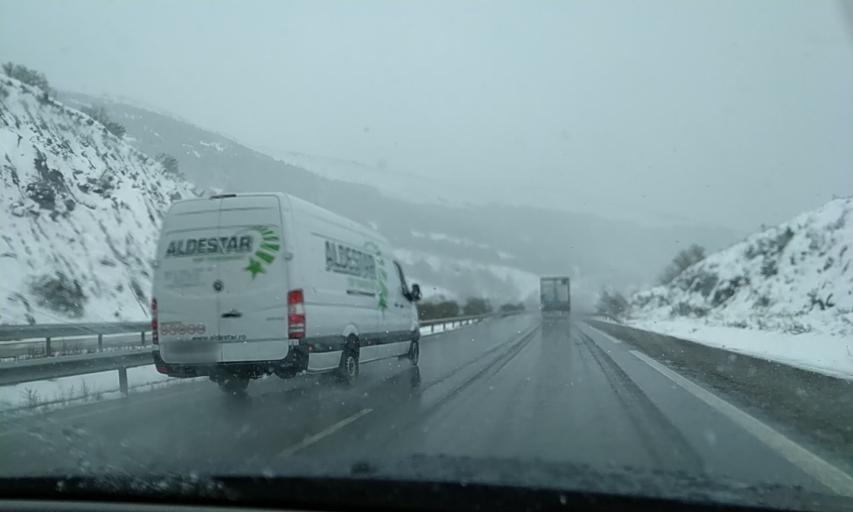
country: ES
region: Castille and Leon
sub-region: Provincia de Zamora
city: Requejo
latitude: 42.0399
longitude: -6.7928
